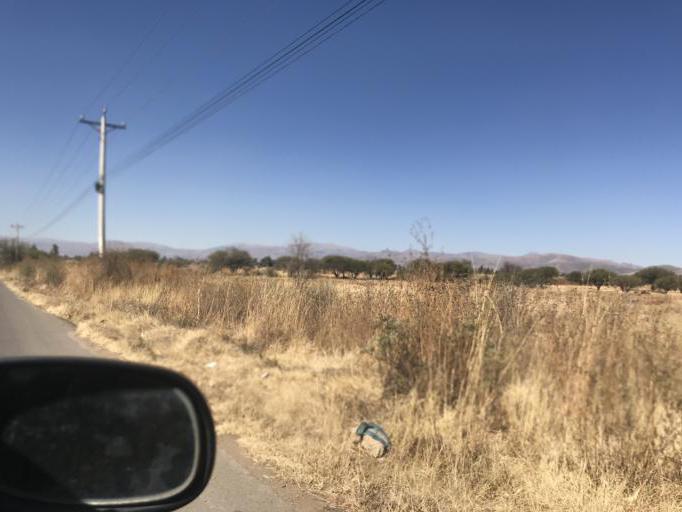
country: BO
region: Cochabamba
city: Cliza
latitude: -17.5994
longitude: -65.9633
